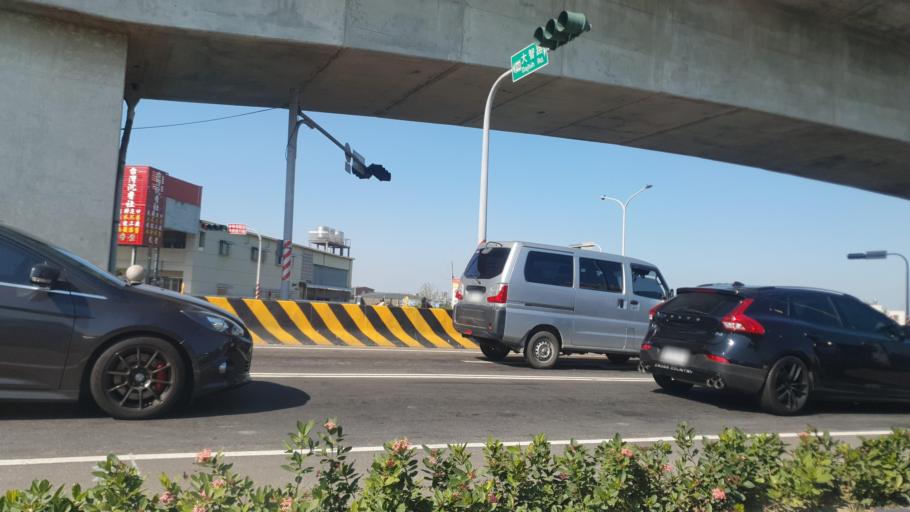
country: TW
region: Taiwan
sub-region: Tainan
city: Tainan
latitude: 23.0232
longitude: 120.2895
